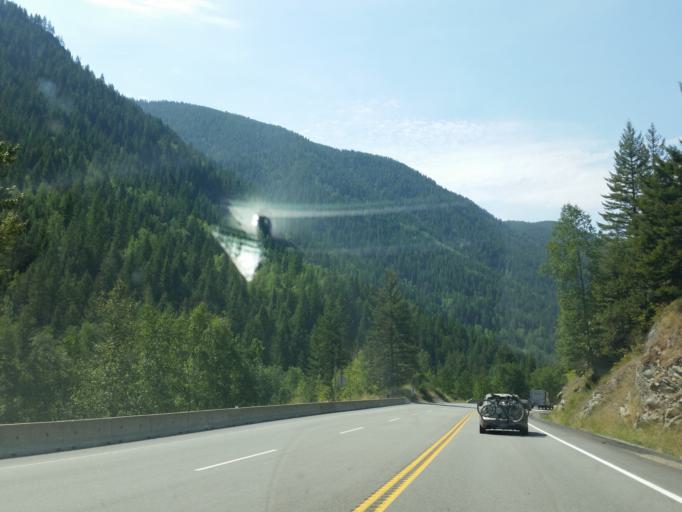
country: CA
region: British Columbia
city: Rossland
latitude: 49.1452
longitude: -118.1192
